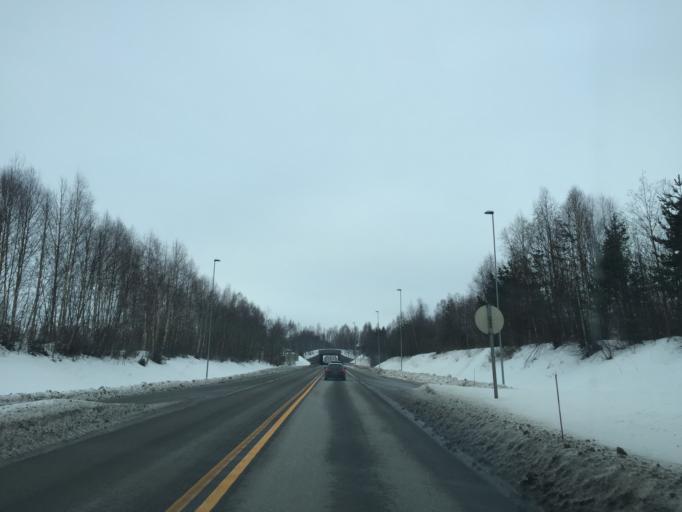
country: NO
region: Hedmark
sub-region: Loten
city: Loten
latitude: 60.7877
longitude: 11.3017
